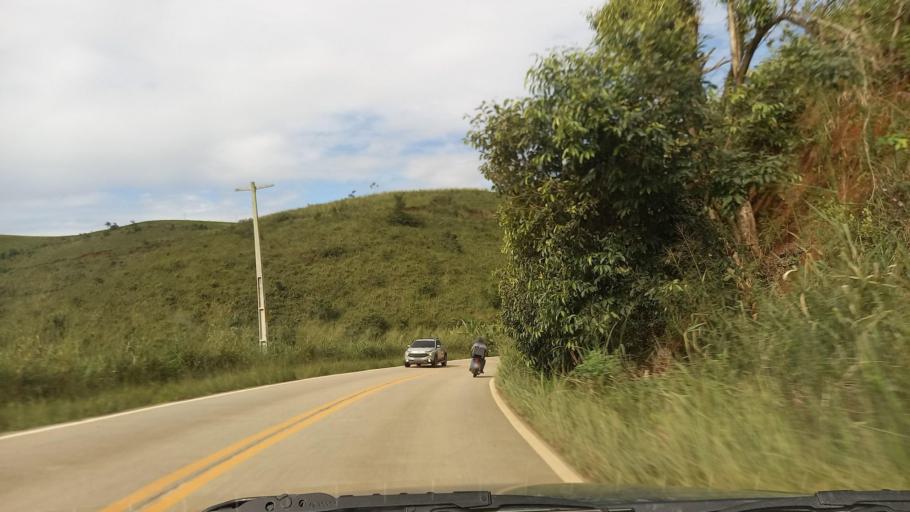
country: BR
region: Pernambuco
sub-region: Maraial
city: Maraial
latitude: -8.7485
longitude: -35.8326
